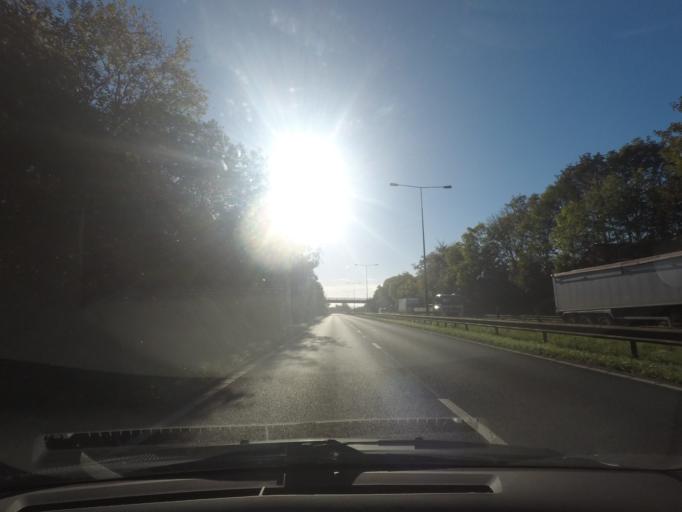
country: GB
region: England
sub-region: East Riding of Yorkshire
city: Brough
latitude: 53.7410
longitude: -0.5648
